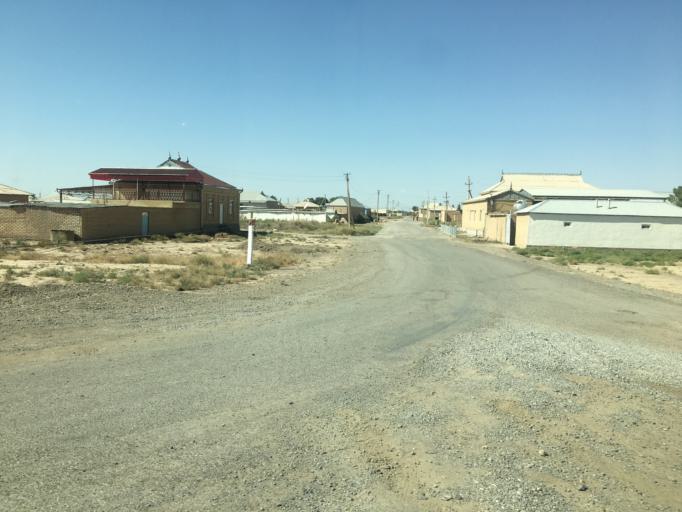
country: IR
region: Razavi Khorasan
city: Sarakhs
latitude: 36.5411
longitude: 61.2184
